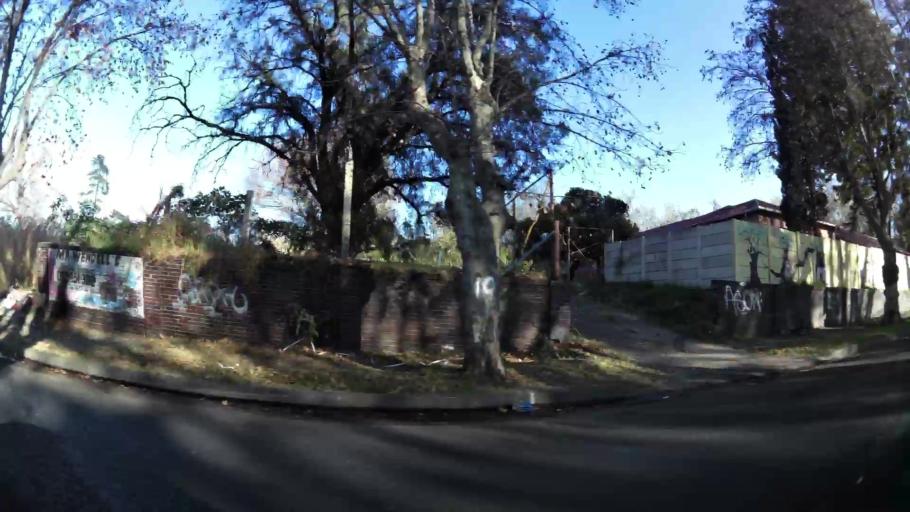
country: ZA
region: Gauteng
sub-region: City of Johannesburg Metropolitan Municipality
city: Johannesburg
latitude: -26.2034
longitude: 27.9905
